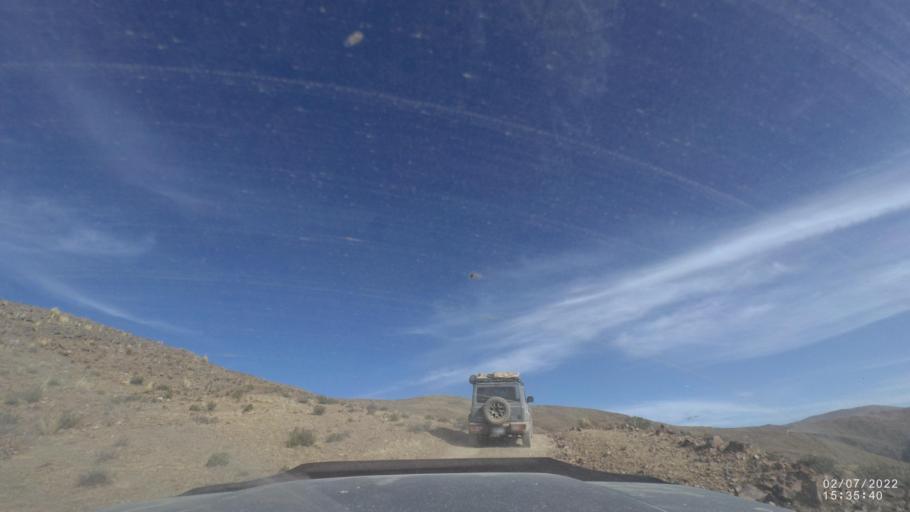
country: BO
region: Cochabamba
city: Irpa Irpa
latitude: -17.8885
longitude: -66.4108
